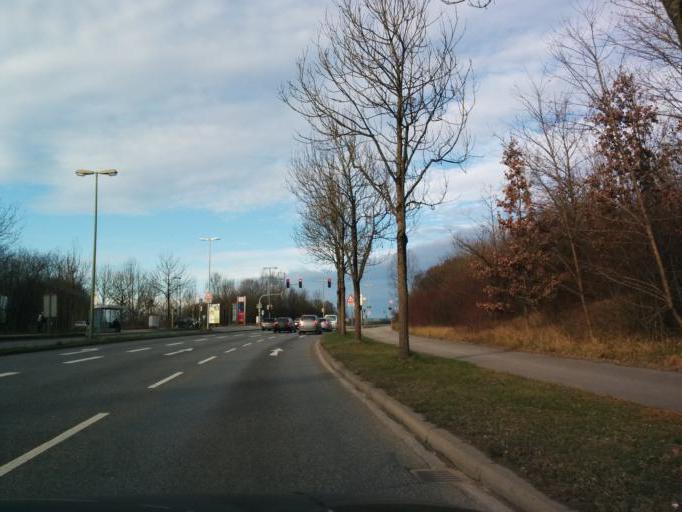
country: DE
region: Bavaria
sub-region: Upper Bavaria
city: Karlsfeld
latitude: 48.1940
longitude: 11.4970
